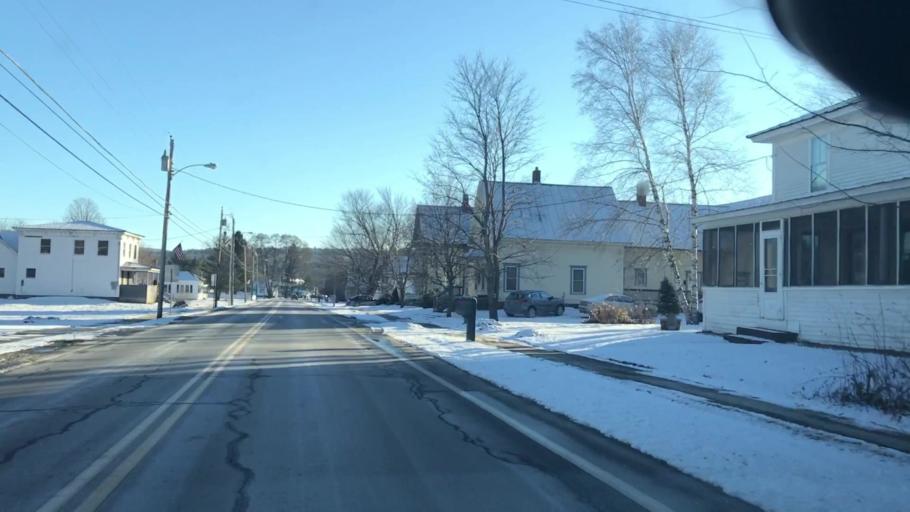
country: US
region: New Hampshire
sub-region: Grafton County
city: North Haverhill
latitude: 44.0876
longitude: -72.0259
